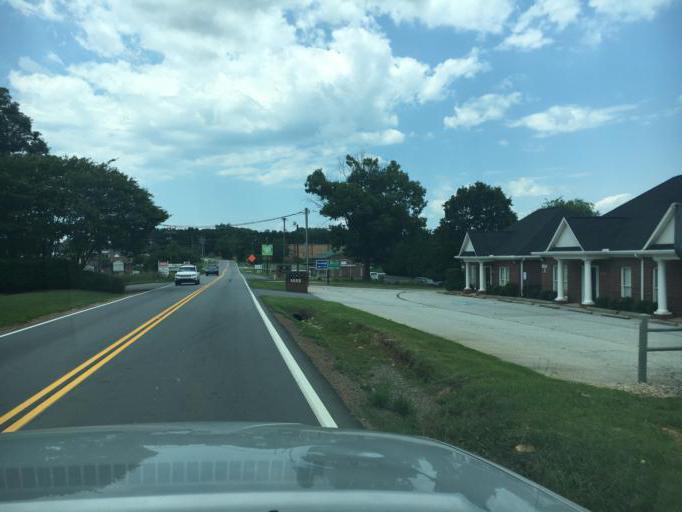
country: US
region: South Carolina
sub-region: Greenville County
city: Five Forks
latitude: 34.8691
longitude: -82.2476
